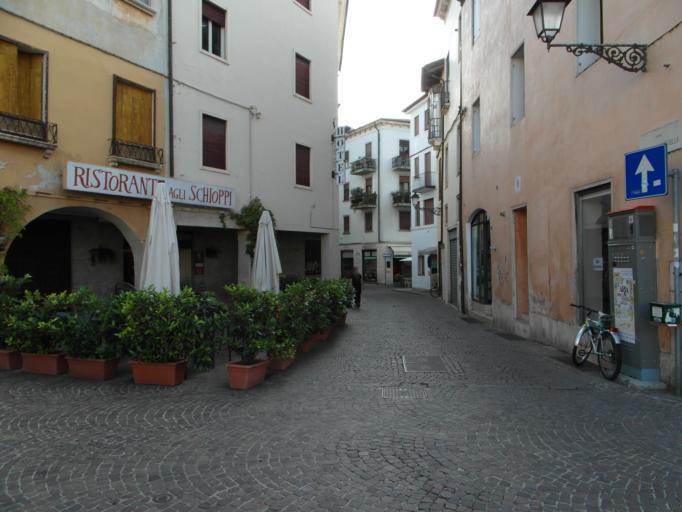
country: IT
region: Veneto
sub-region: Provincia di Vicenza
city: Vicenza
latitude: 45.5459
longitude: 11.5420
